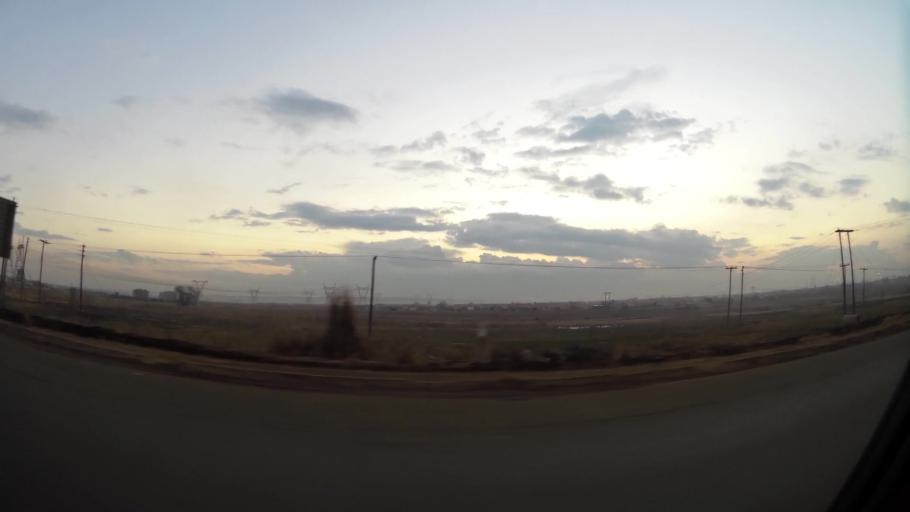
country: ZA
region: Gauteng
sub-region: City of Johannesburg Metropolitan Municipality
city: Orange Farm
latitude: -26.5486
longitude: 27.8305
